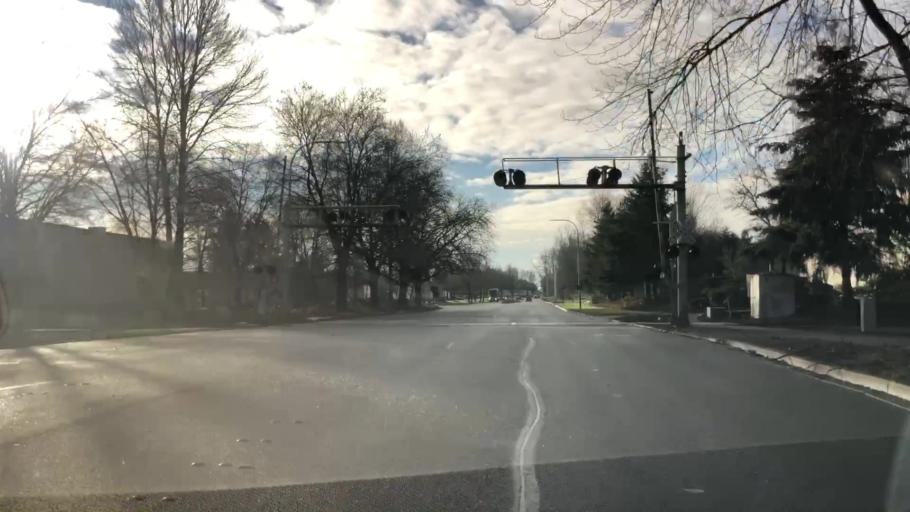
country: US
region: Washington
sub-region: King County
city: Tukwila
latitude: 47.4451
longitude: -122.2328
